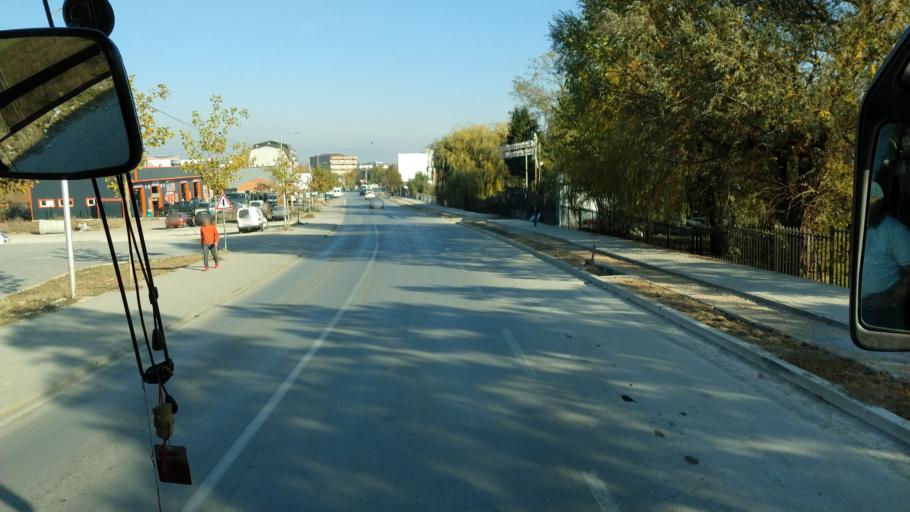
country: XK
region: Ferizaj
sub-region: Komuna e Shtimes
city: Shtime
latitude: 42.4353
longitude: 21.0286
